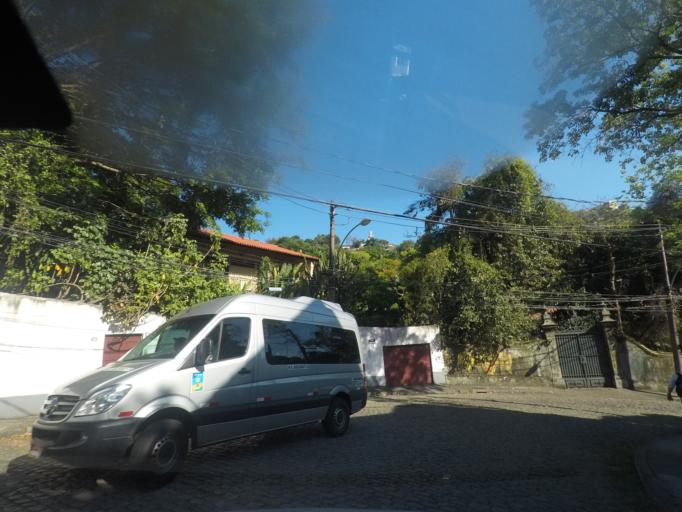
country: BR
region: Rio de Janeiro
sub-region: Rio De Janeiro
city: Rio de Janeiro
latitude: -22.9414
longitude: -43.2054
